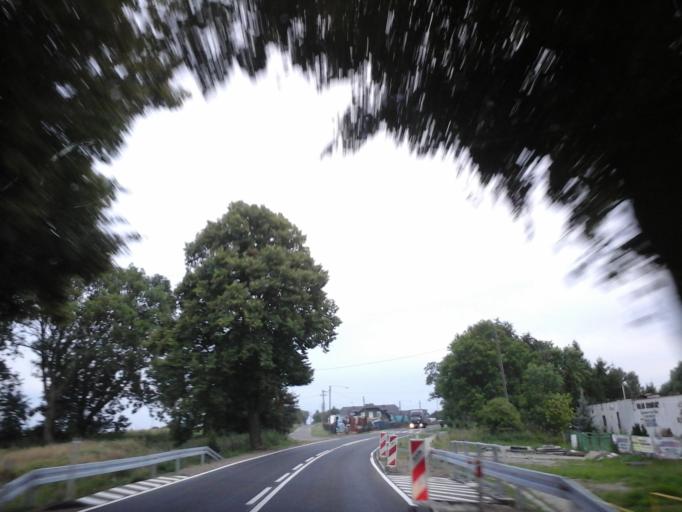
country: PL
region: West Pomeranian Voivodeship
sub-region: Powiat goleniowski
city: Maszewo
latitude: 53.4884
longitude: 15.0641
